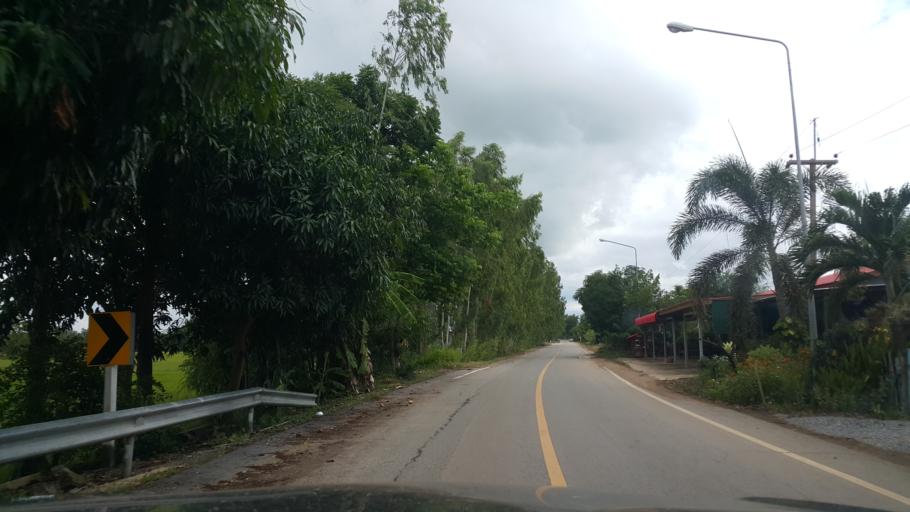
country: TH
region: Sukhothai
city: Kong Krailat
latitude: 16.9272
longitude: 99.9058
